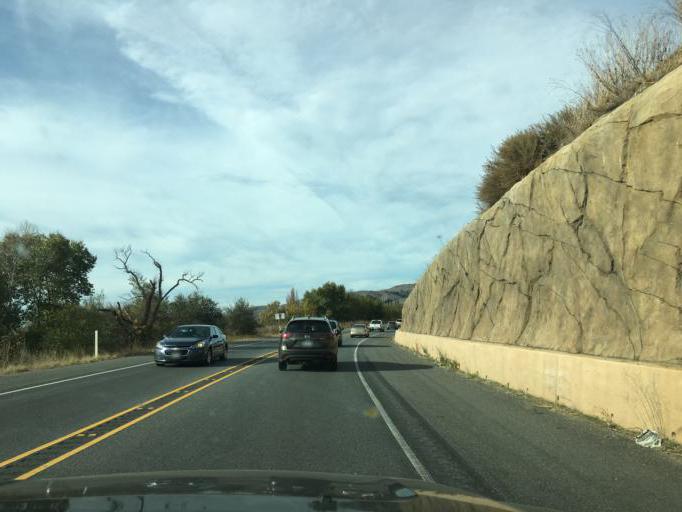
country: US
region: California
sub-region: San Benito County
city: Hollister
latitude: 36.9730
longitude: -121.4333
